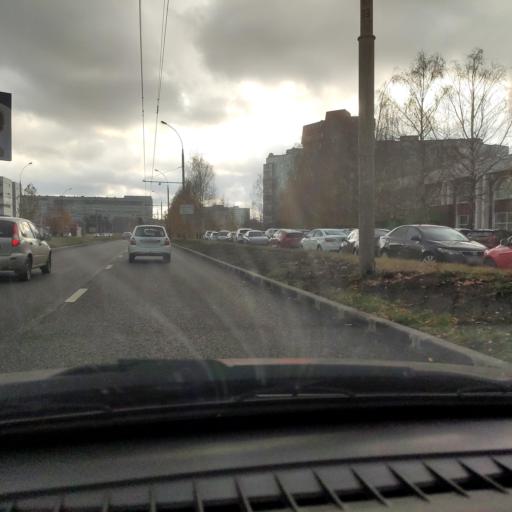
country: RU
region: Samara
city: Tol'yatti
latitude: 53.5278
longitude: 49.3271
